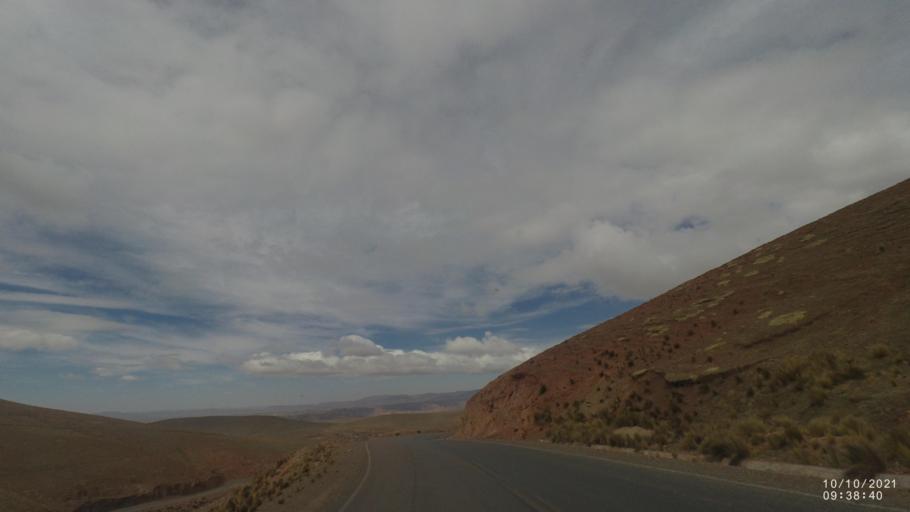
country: BO
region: La Paz
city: Quime
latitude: -17.1353
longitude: -67.3397
